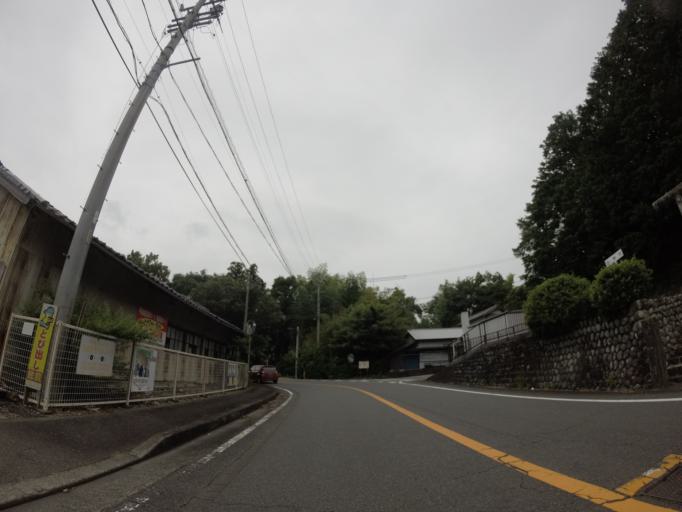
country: JP
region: Shizuoka
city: Shimada
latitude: 34.8108
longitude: 138.1668
